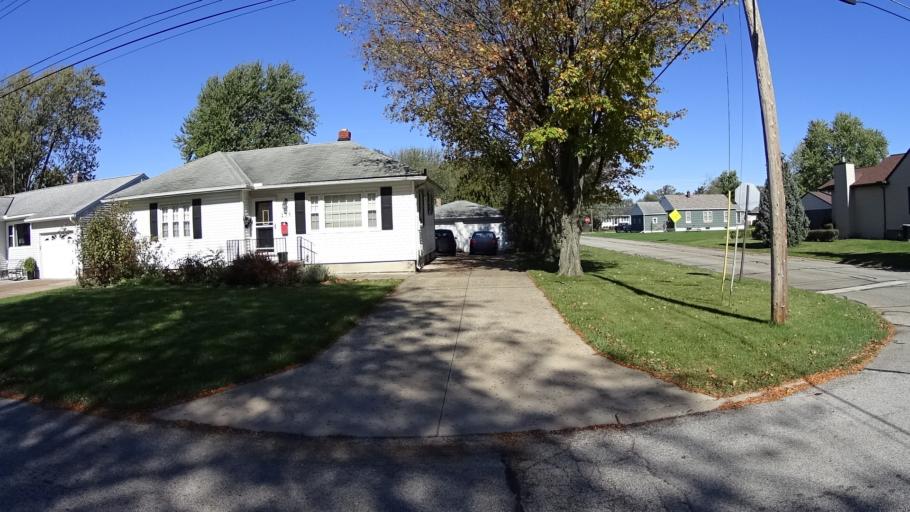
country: US
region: Ohio
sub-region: Lorain County
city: Amherst
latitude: 41.4044
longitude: -82.2261
